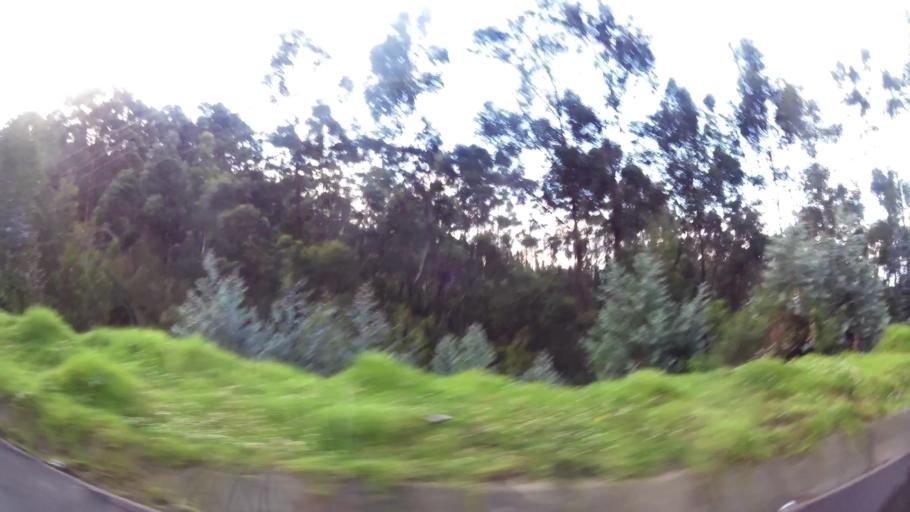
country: EC
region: Pichincha
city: Quito
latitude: -0.1097
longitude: -78.5210
